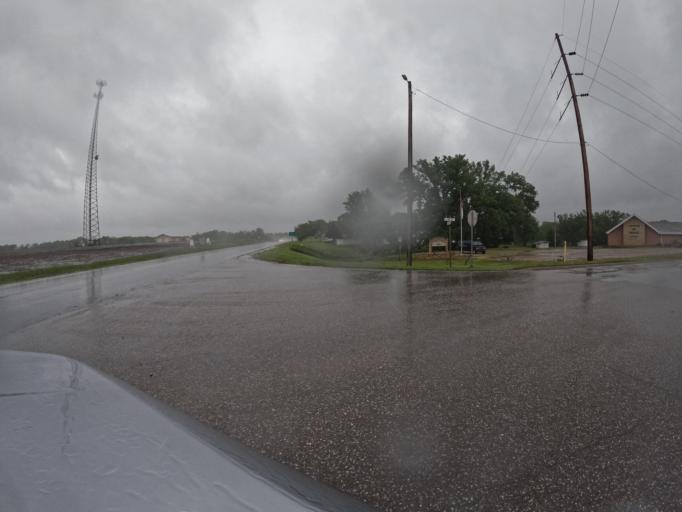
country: US
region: Nebraska
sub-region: Gage County
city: Wymore
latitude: 40.1286
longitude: -96.6707
